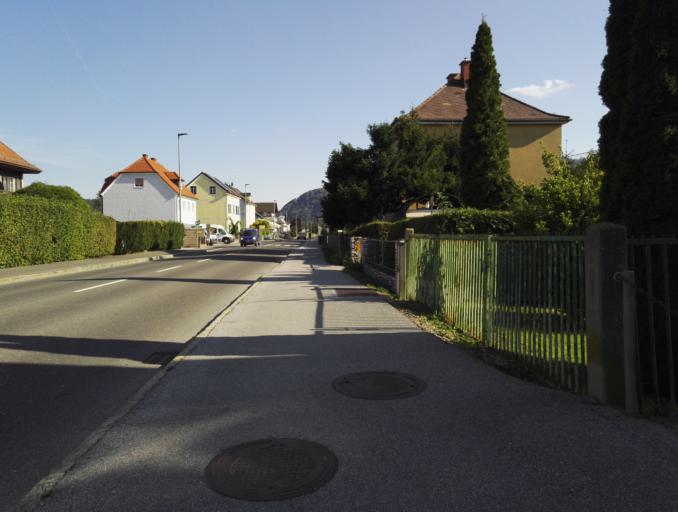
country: AT
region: Styria
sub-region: Politischer Bezirk Graz-Umgebung
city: Gratkorn
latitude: 47.1312
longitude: 15.3409
